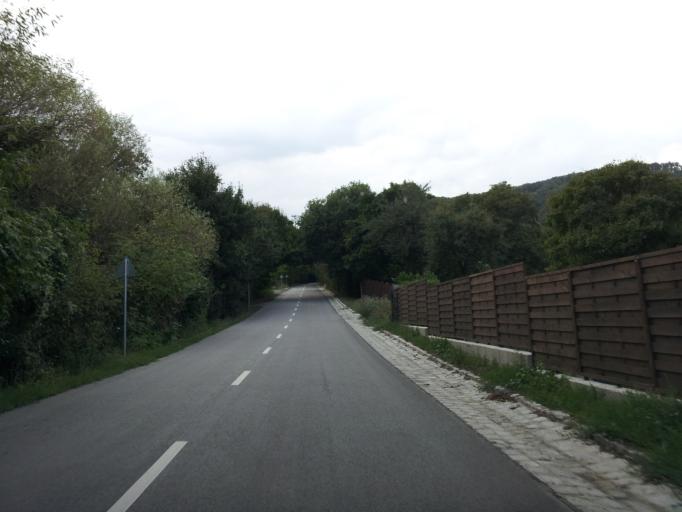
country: HU
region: Pest
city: Kismaros
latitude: 47.8305
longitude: 18.9679
